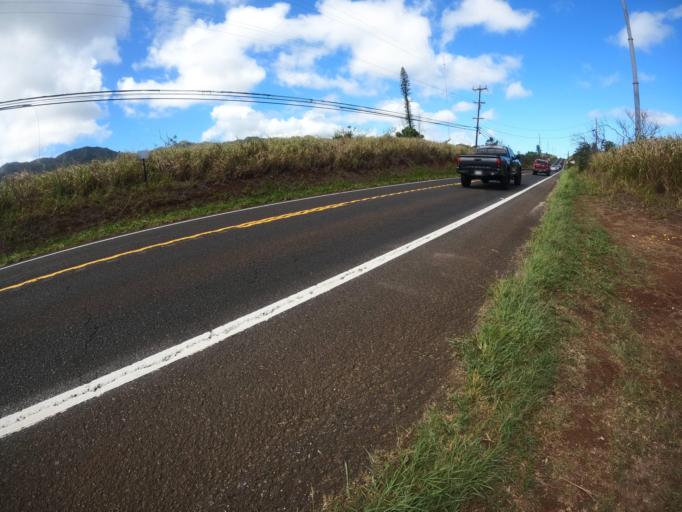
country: US
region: Hawaii
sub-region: Honolulu County
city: Village Park
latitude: 21.4407
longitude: -158.0596
